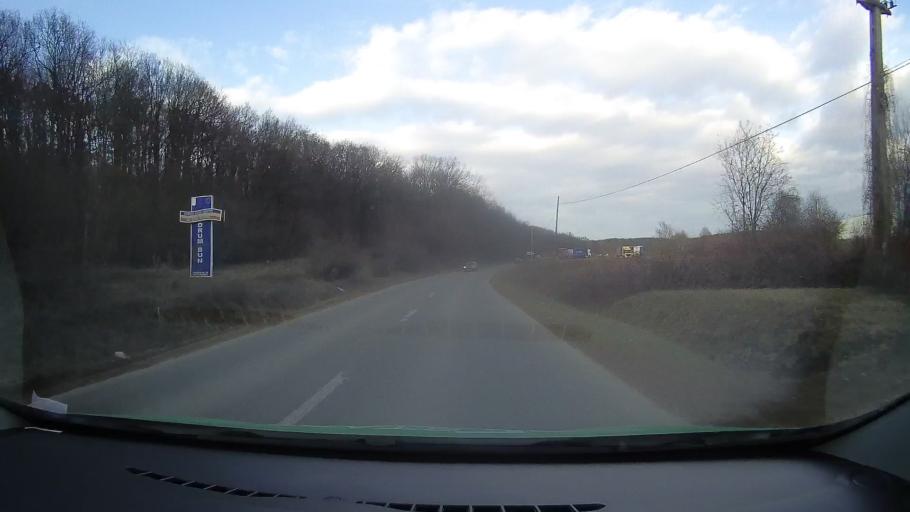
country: RO
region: Dambovita
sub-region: Comuna Gura Ocnitei
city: Gura Ocnitei
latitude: 44.9449
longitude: 25.5852
